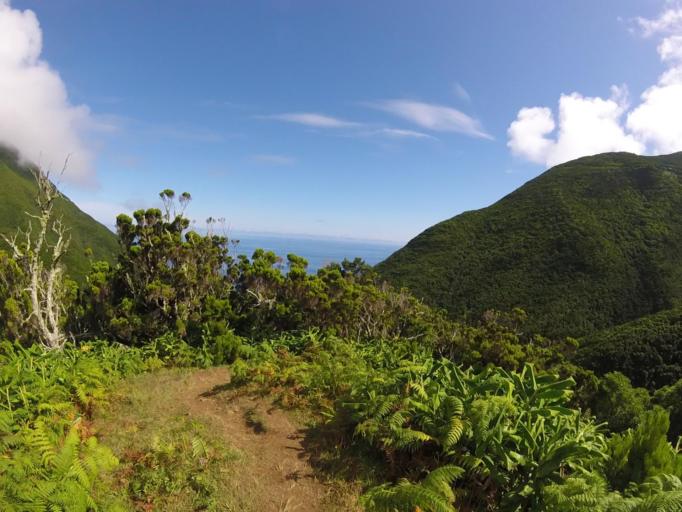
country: PT
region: Azores
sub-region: Sao Roque do Pico
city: Sao Roque do Pico
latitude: 38.6079
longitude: -27.9202
